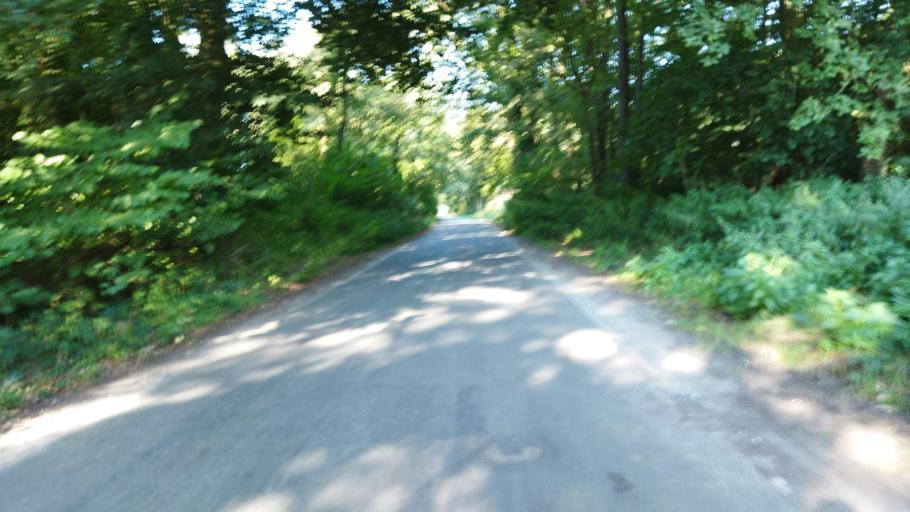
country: DE
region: Lower Saxony
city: Bad Laer
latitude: 52.1197
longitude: 8.0637
